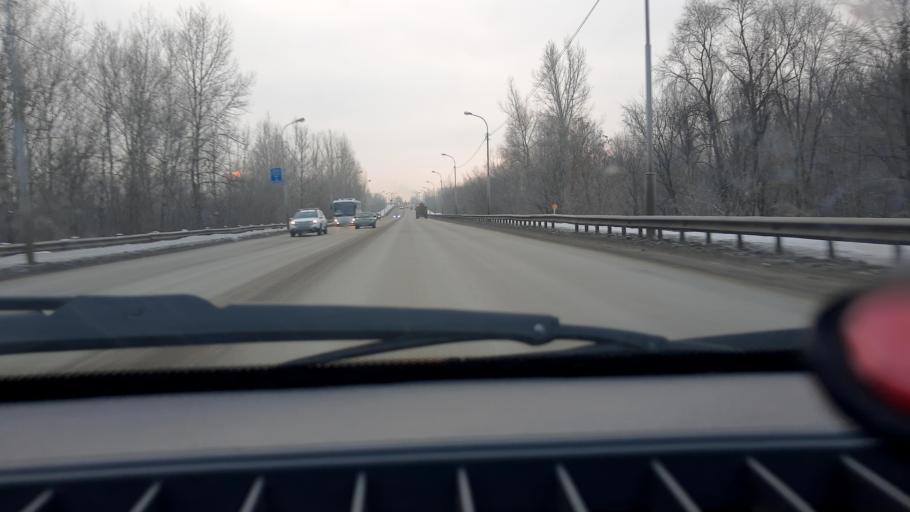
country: RU
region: Bashkortostan
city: Iglino
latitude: 54.7929
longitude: 56.2104
